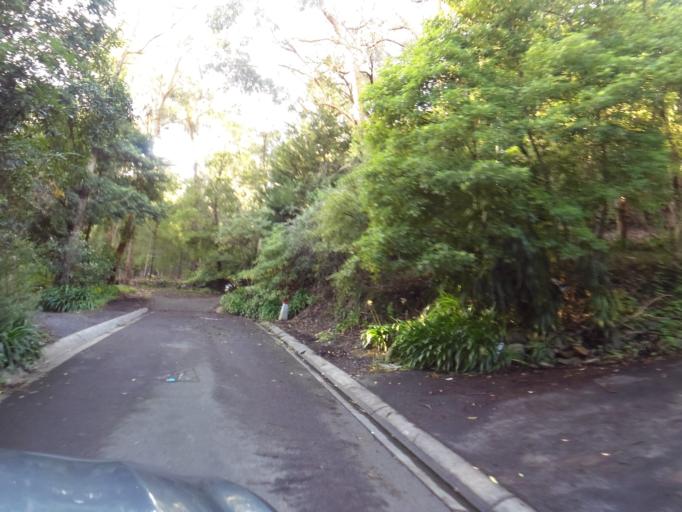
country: AU
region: Victoria
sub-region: Knox
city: Ferntree Gully
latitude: -37.8889
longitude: 145.3070
